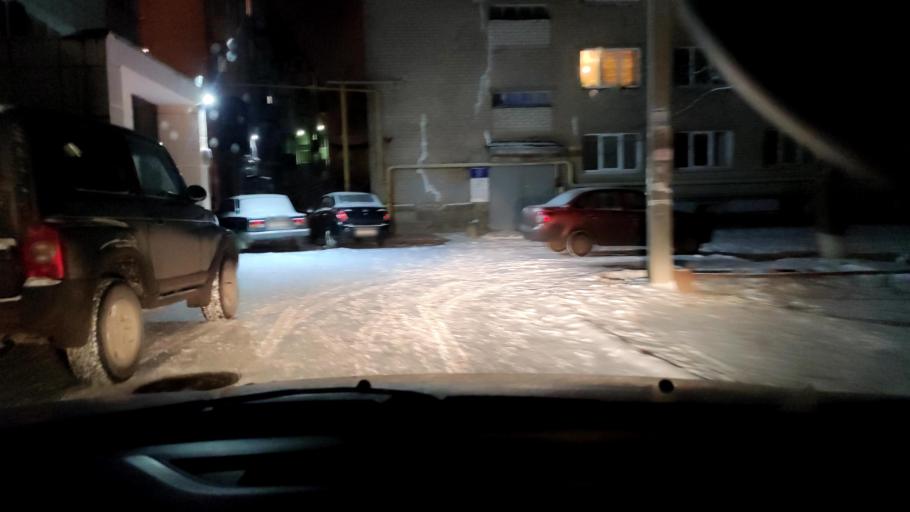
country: RU
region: Perm
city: Kultayevo
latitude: 58.0095
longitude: 55.9655
